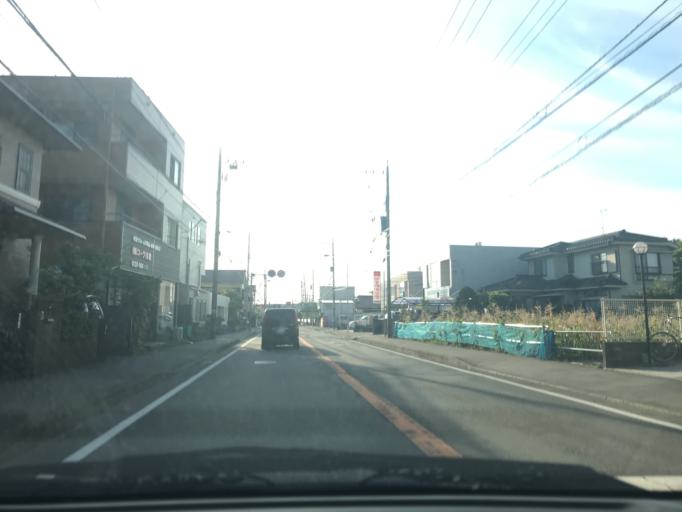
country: JP
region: Kanagawa
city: Fujisawa
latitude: 35.3421
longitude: 139.4727
